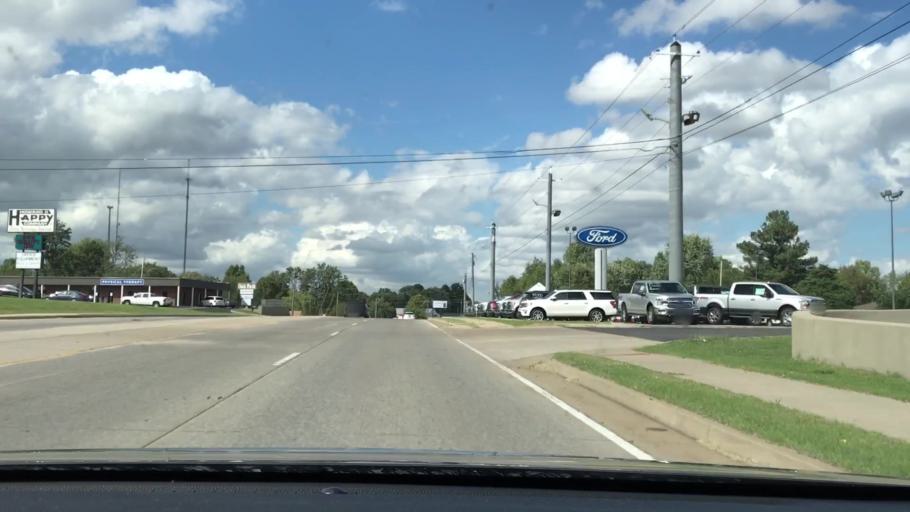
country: US
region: Kentucky
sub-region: Graves County
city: Mayfield
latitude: 36.7602
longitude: -88.6419
